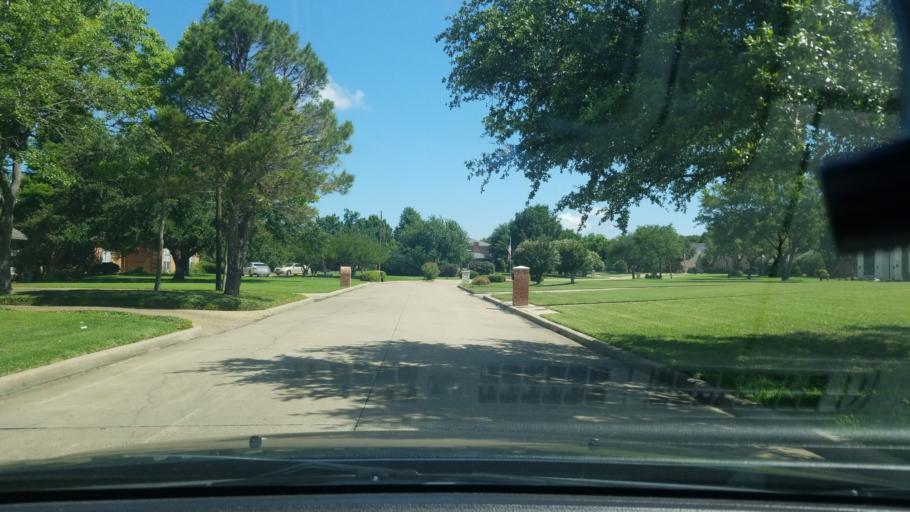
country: US
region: Texas
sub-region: Dallas County
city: Sunnyvale
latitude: 32.7999
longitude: -96.5891
